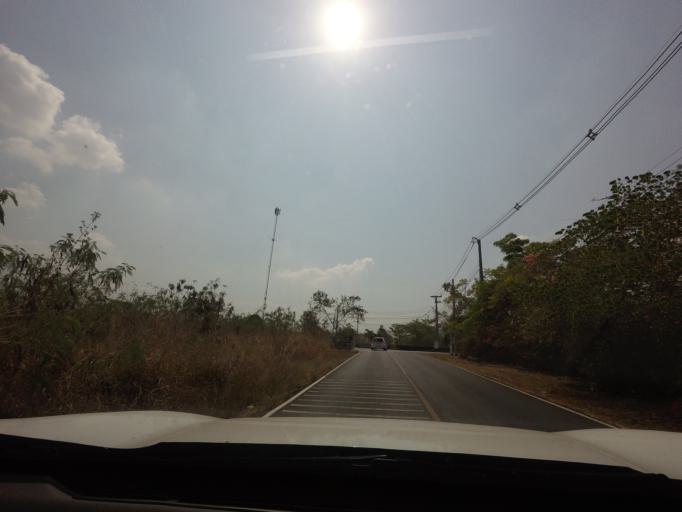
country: TH
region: Nakhon Ratchasima
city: Pak Chong
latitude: 14.5781
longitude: 101.4365
